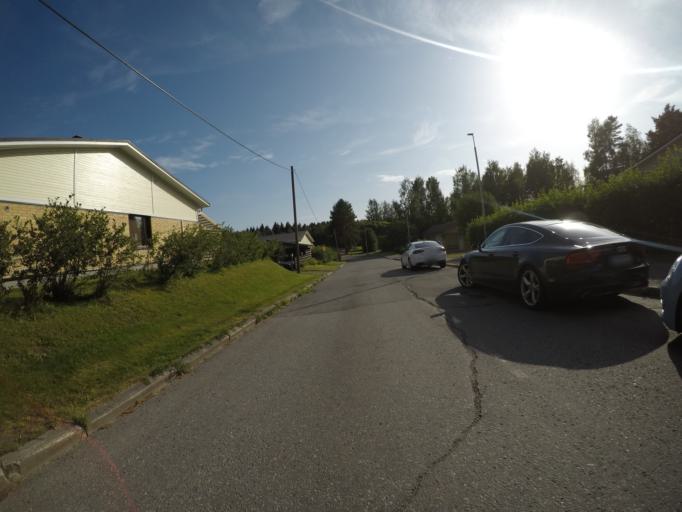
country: FI
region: Haeme
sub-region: Haemeenlinna
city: Haemeenlinna
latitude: 60.9791
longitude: 24.3996
